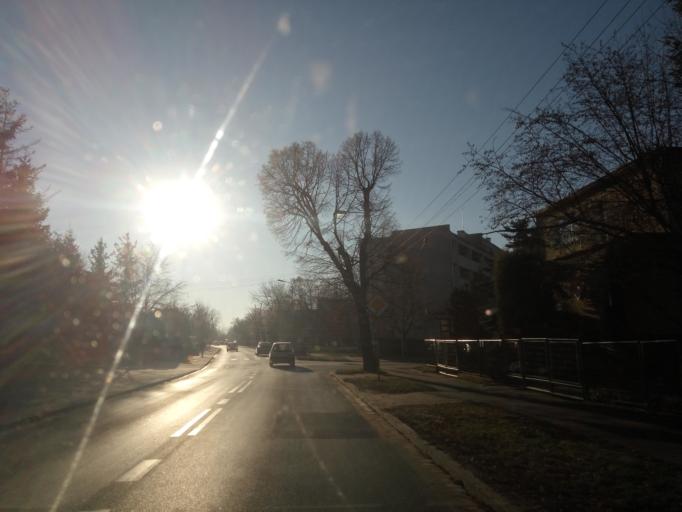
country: PL
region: Lower Silesian Voivodeship
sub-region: Powiat wroclawski
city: Wroclaw
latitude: 51.1262
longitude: 16.9524
